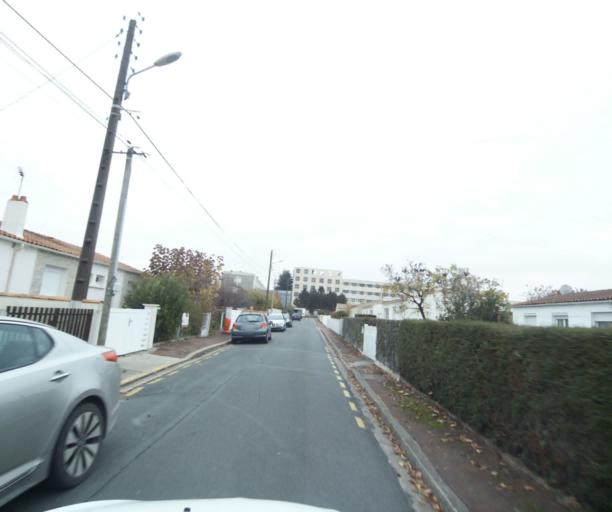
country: FR
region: Poitou-Charentes
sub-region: Departement de la Charente-Maritime
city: Saintes
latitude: 45.7367
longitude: -0.6164
